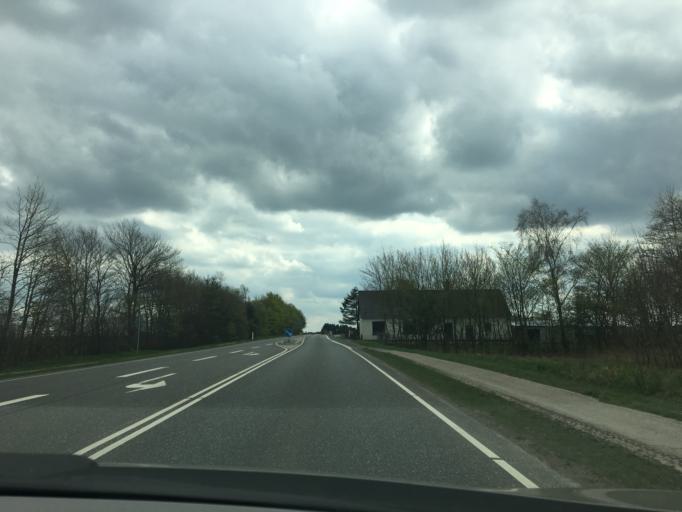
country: DK
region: Central Jutland
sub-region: Horsens Kommune
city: Braedstrup
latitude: 56.0212
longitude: 9.6089
